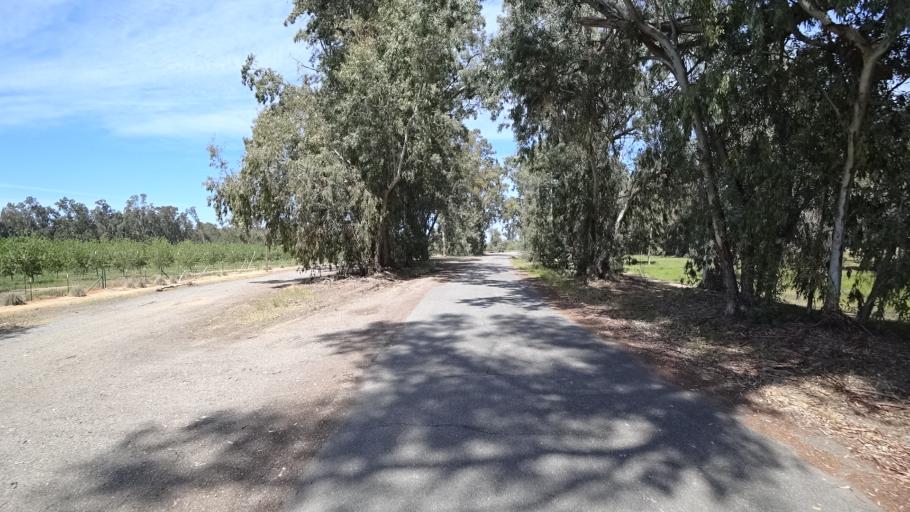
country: US
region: California
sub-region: Glenn County
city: Willows
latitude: 39.5868
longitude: -122.1955
